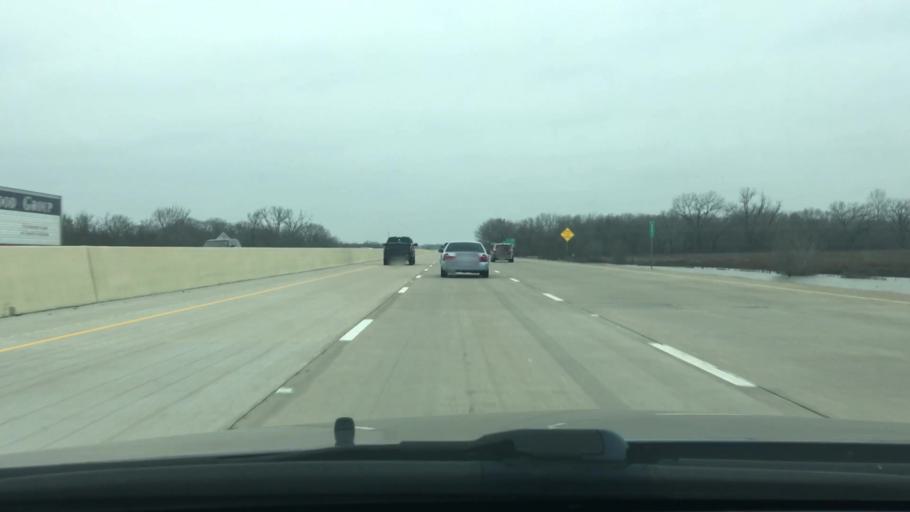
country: US
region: Texas
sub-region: Navarro County
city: Corsicana
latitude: 31.9529
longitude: -96.4213
